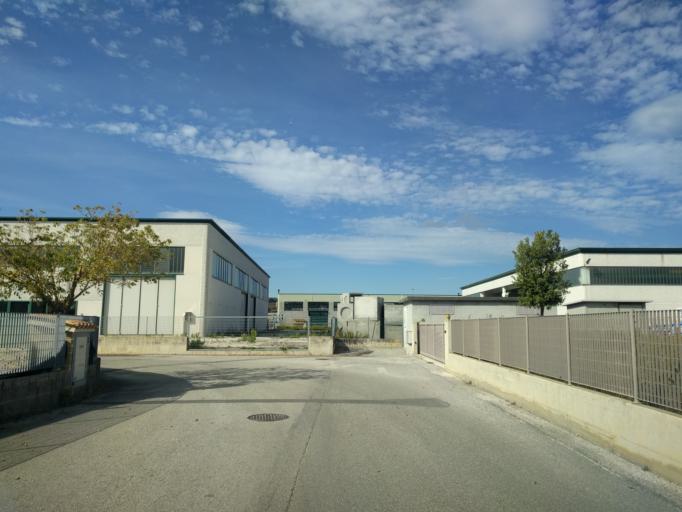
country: IT
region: The Marches
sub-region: Provincia di Pesaro e Urbino
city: Lucrezia
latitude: 43.7613
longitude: 12.9351
